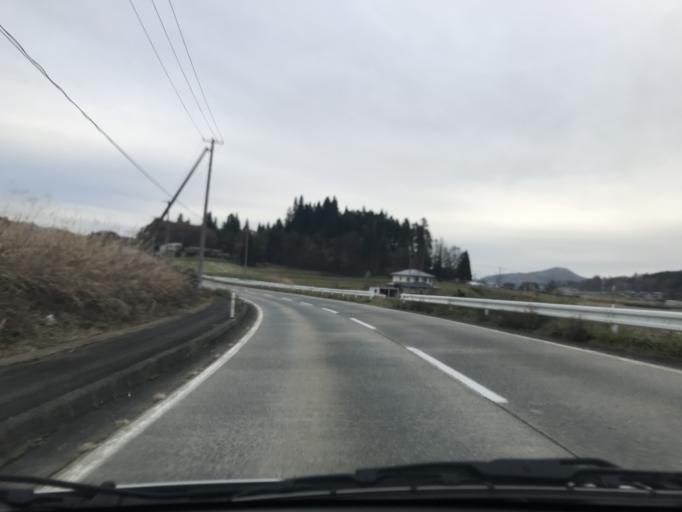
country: JP
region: Iwate
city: Kitakami
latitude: 39.2914
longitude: 141.2129
